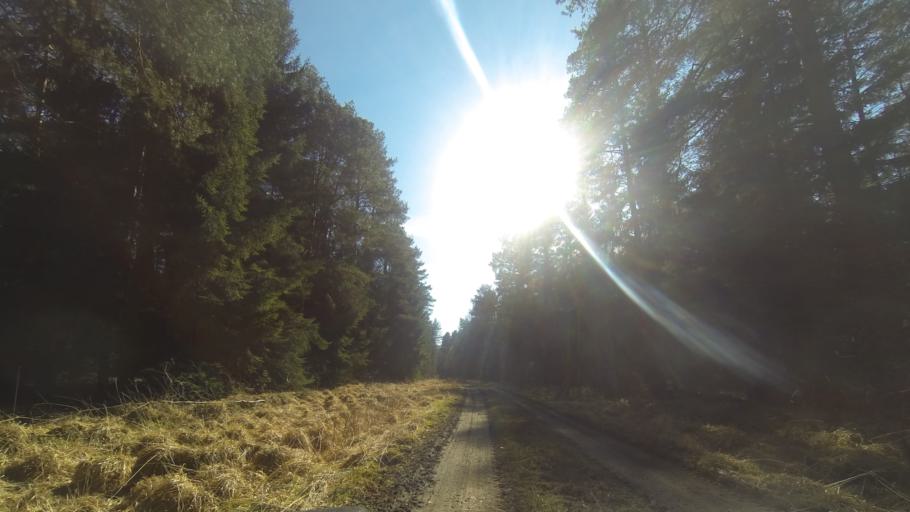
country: DE
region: Saxony
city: Laussnitz
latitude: 51.2563
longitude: 13.8460
